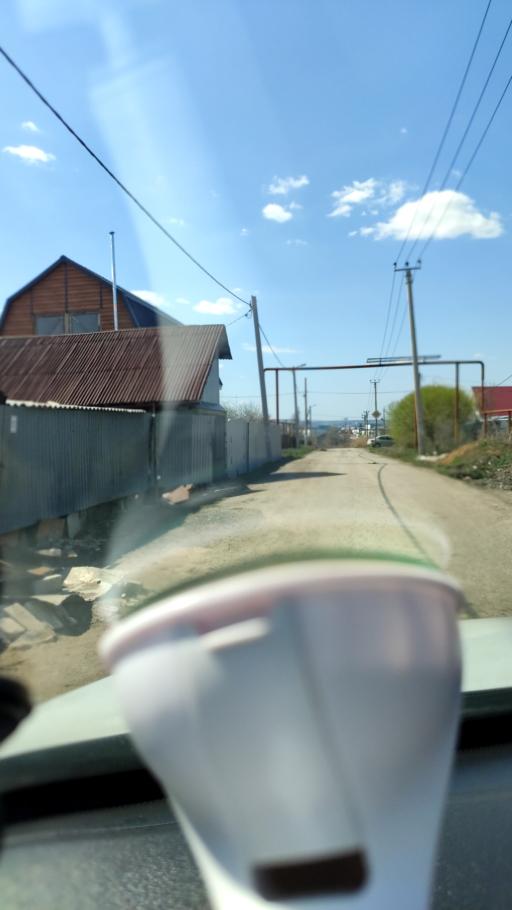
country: RU
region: Samara
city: Smyshlyayevka
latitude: 53.2647
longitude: 50.4149
